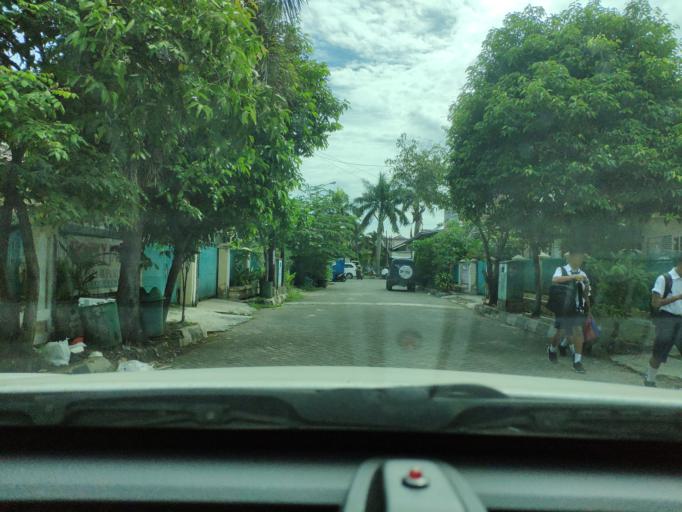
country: ID
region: West Java
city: Ciputat
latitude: -6.2196
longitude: 106.7093
